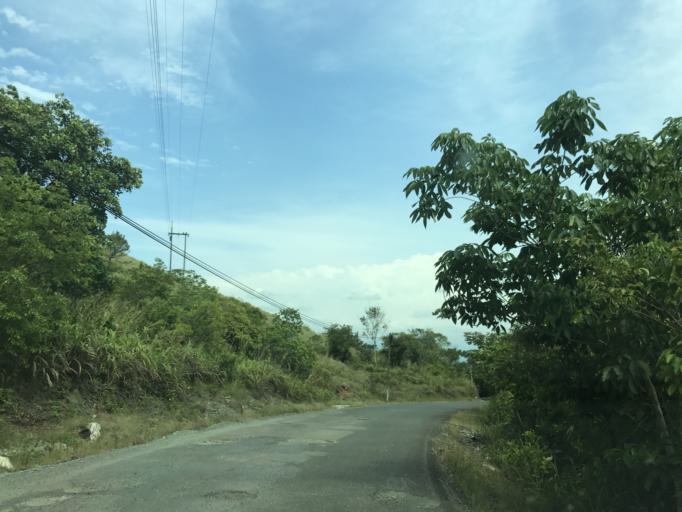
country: GT
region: Izabal
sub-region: Municipio de Los Amates
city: Los Amates
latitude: 15.3864
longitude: -89.0251
